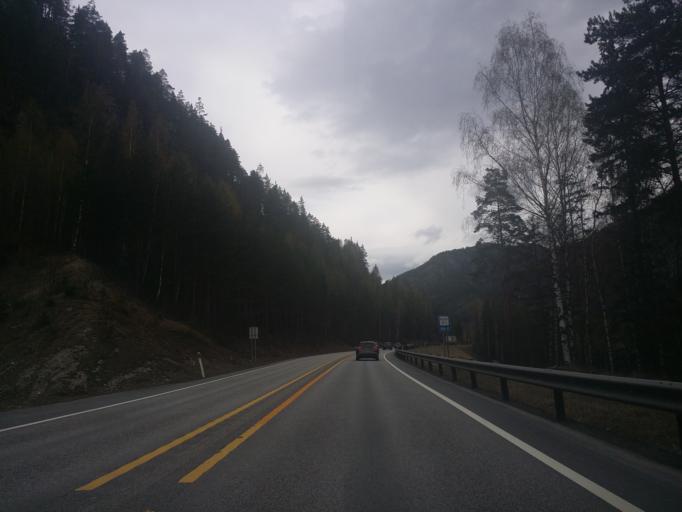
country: NO
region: Buskerud
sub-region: Fla
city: Fla
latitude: 60.4405
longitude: 9.3139
